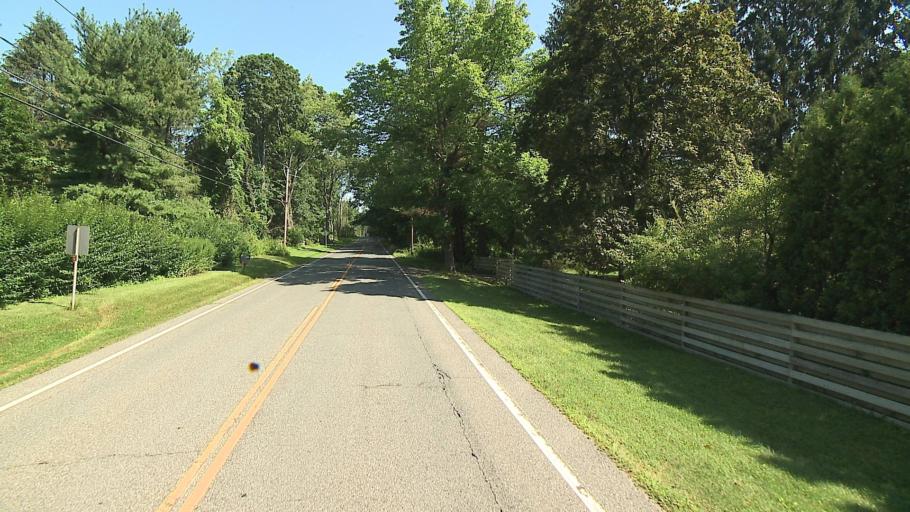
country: US
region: Connecticut
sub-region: Litchfield County
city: Canaan
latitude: 42.0312
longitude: -73.4284
